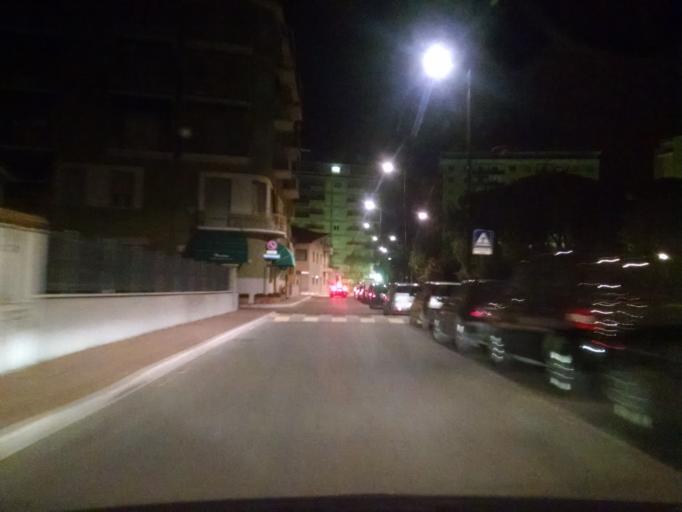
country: IT
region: Tuscany
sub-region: Provincia di Grosseto
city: Follonica
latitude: 42.9245
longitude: 10.7530
